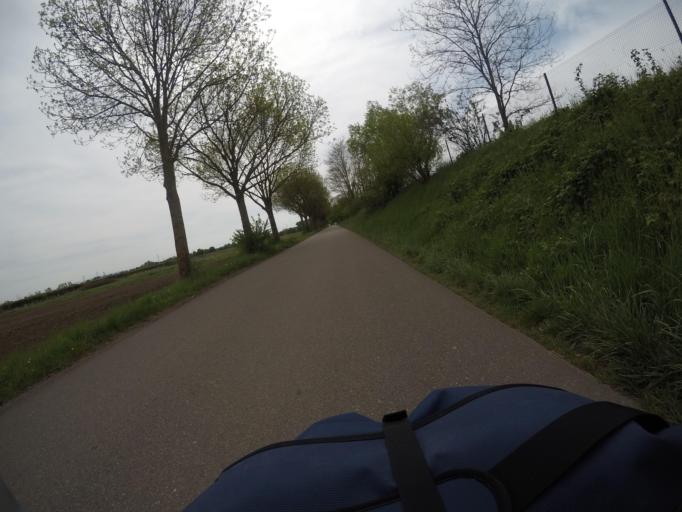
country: DE
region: Baden-Wuerttemberg
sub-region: Freiburg Region
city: Kehl
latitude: 48.5849
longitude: 7.8396
